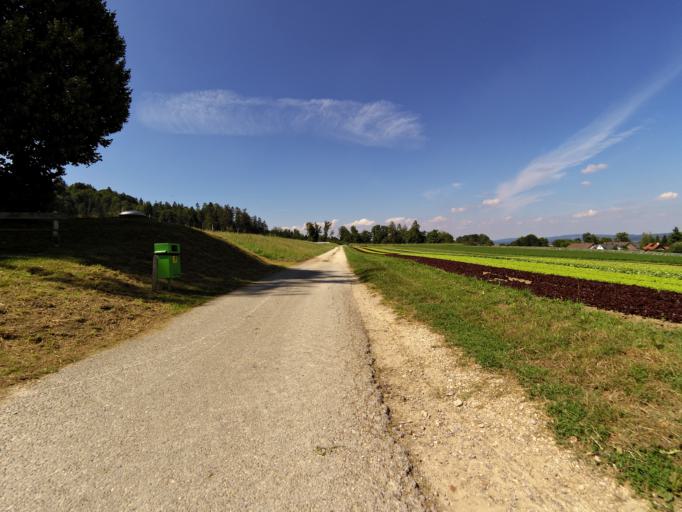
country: CH
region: Thurgau
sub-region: Kreuzlingen District
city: Tagerwilen
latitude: 47.6506
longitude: 9.1255
